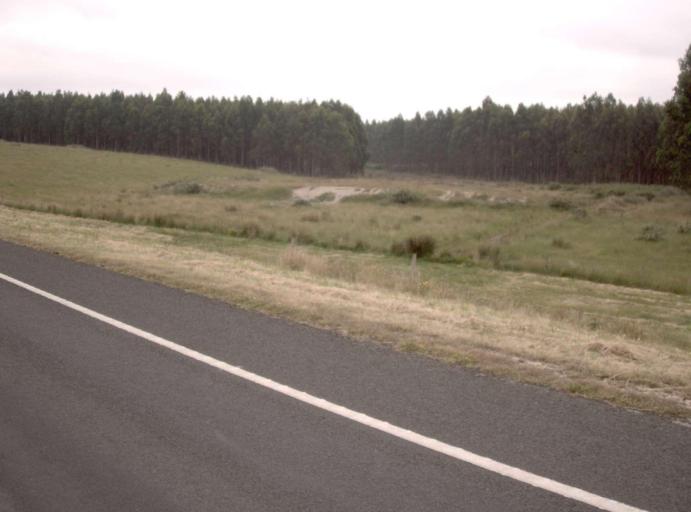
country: AU
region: Victoria
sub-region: Latrobe
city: Morwell
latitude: -38.2439
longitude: 146.3360
